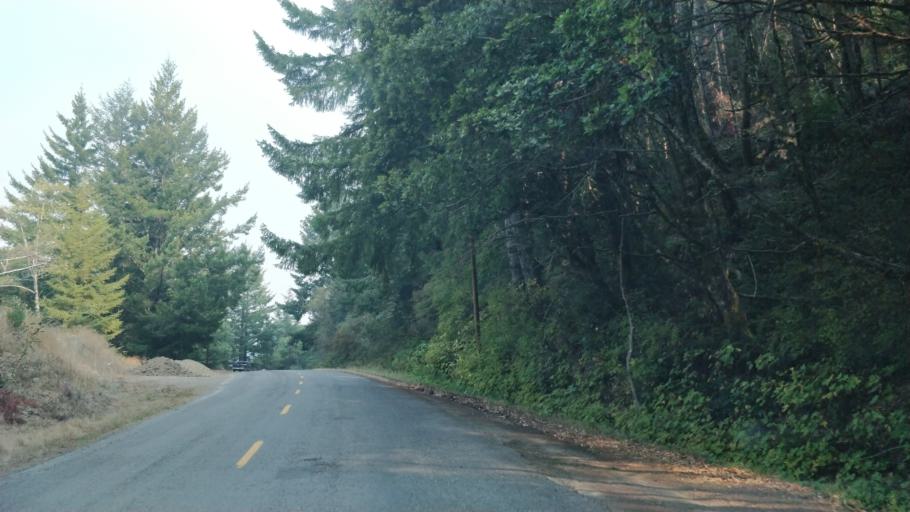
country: US
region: California
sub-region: Humboldt County
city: Rio Dell
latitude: 40.3110
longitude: -124.2777
